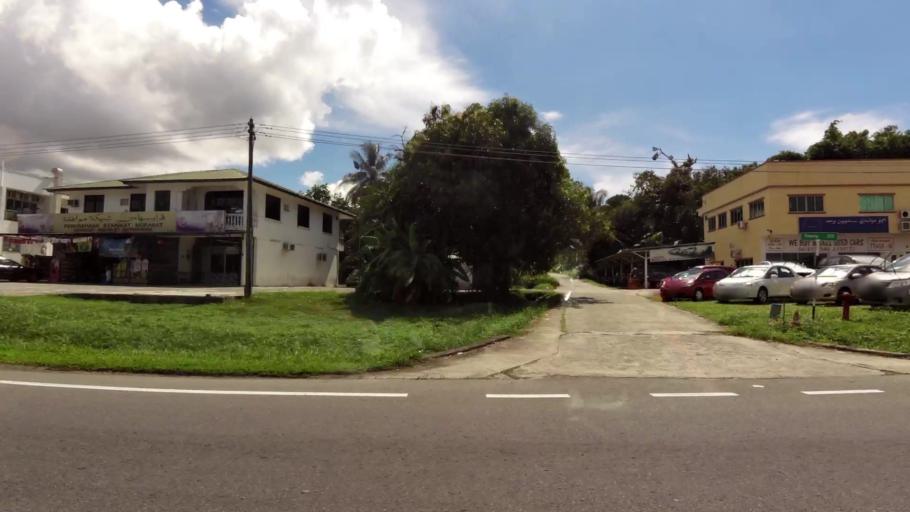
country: BN
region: Brunei and Muara
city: Bandar Seri Begawan
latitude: 4.9700
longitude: 114.9457
